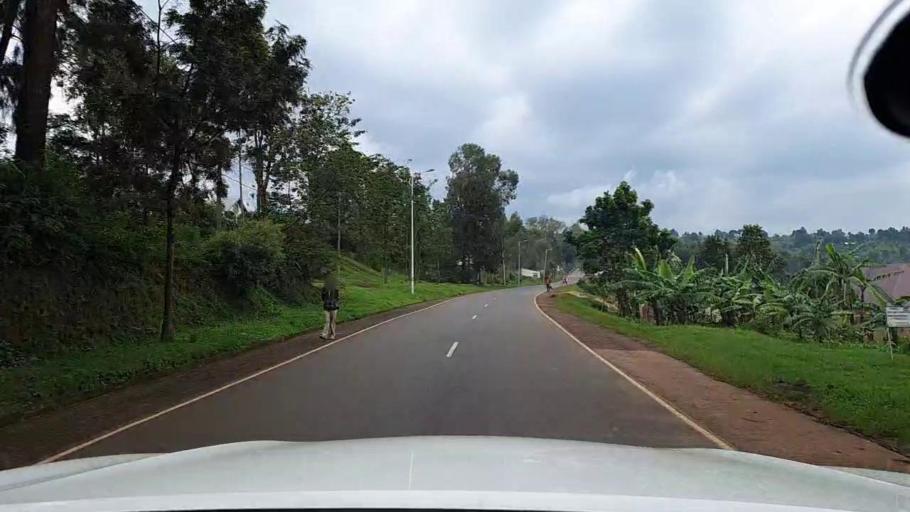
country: RW
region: Western Province
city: Cyangugu
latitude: -2.5371
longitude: 28.8938
